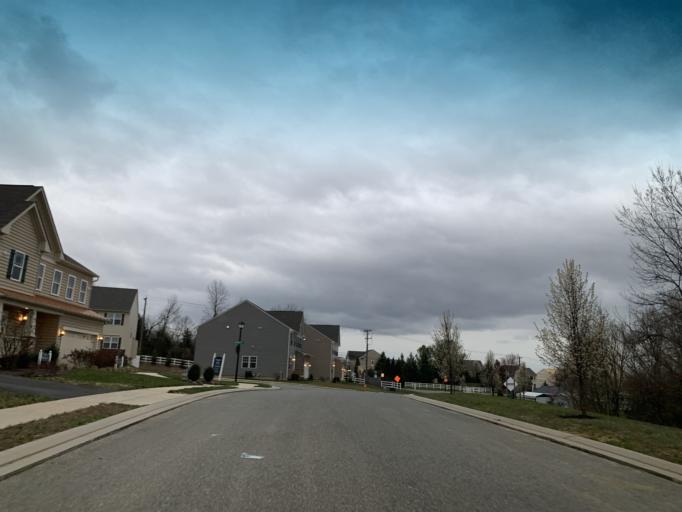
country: US
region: Maryland
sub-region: Harford County
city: Perryman
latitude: 39.5015
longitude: -76.2097
